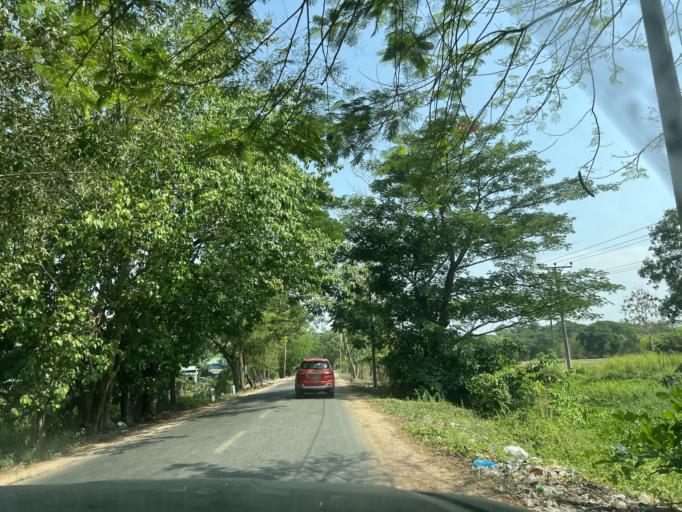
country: MM
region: Yangon
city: Yangon
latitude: 16.9367
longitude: 95.9689
